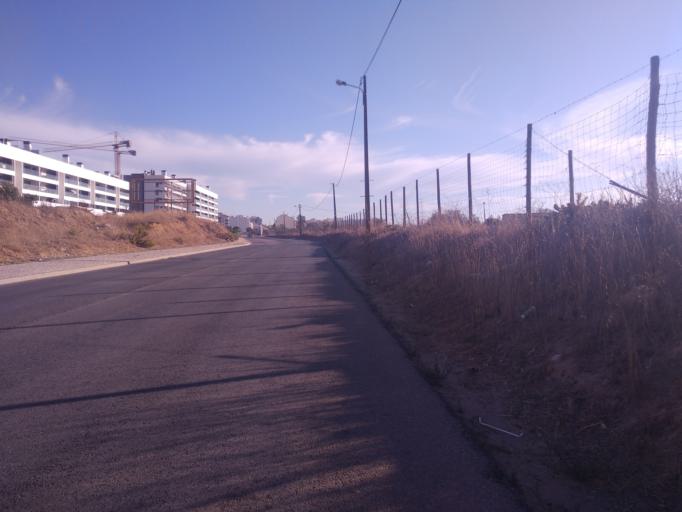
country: PT
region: Faro
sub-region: Faro
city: Faro
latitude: 37.0326
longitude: -7.9399
